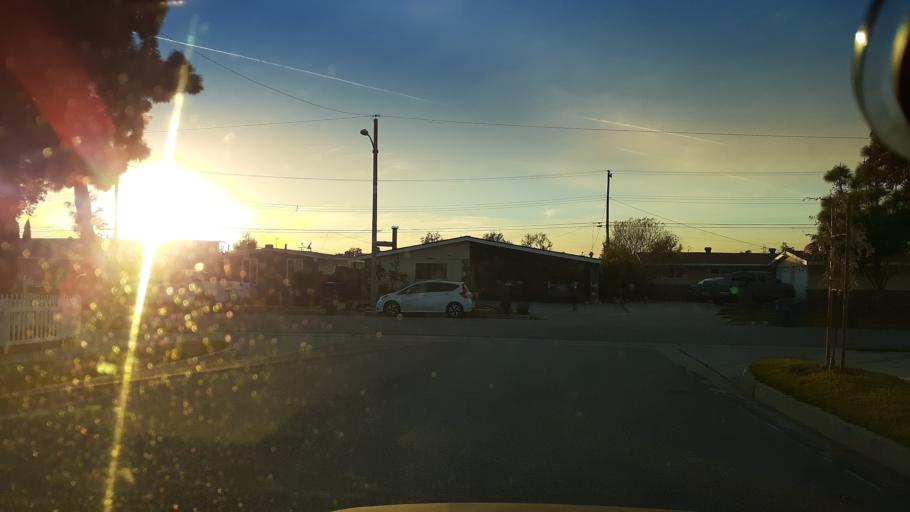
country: US
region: California
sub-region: Los Angeles County
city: Artesia
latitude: 33.8472
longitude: -118.0857
